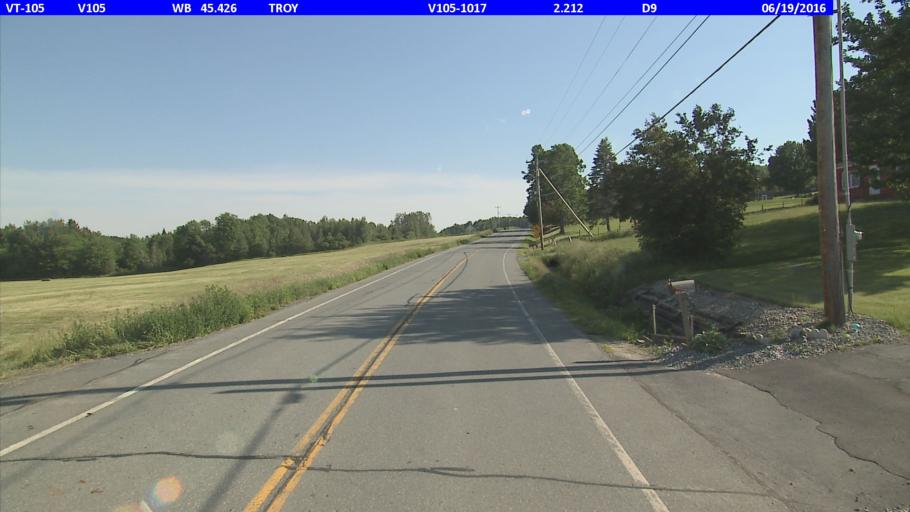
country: US
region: Vermont
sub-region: Orleans County
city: Newport
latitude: 44.9901
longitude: -72.4080
